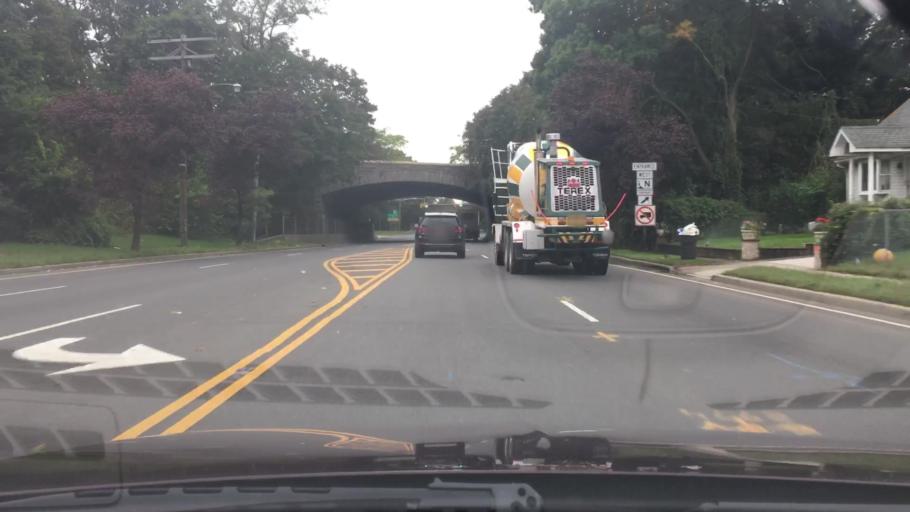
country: US
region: New York
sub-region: Nassau County
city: New Cassel
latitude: 40.7721
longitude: -73.5632
